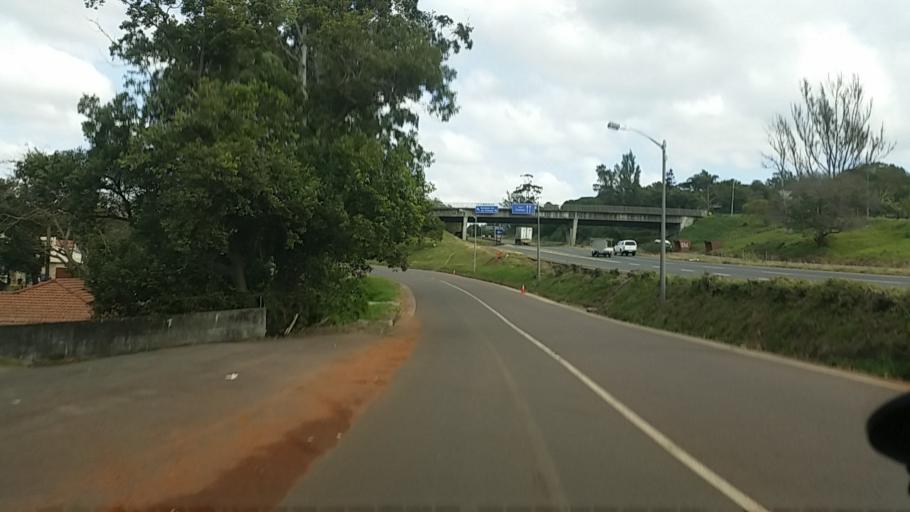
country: ZA
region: KwaZulu-Natal
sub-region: eThekwini Metropolitan Municipality
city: Berea
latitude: -29.8310
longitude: 30.9428
